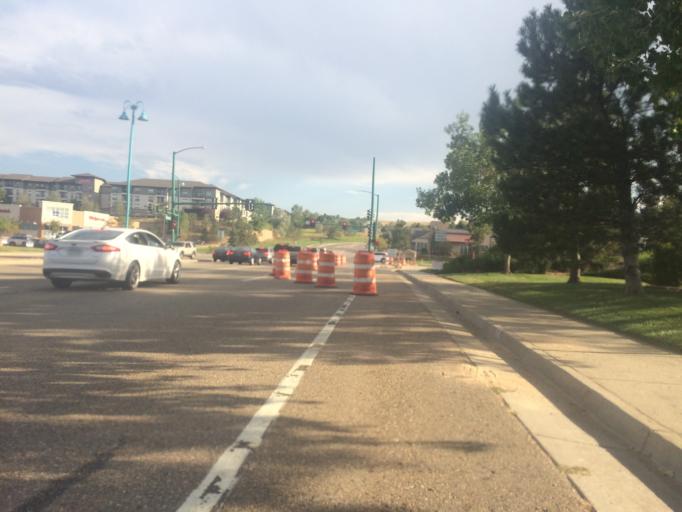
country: US
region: Colorado
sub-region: Boulder County
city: Superior
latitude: 39.9296
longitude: -105.1475
